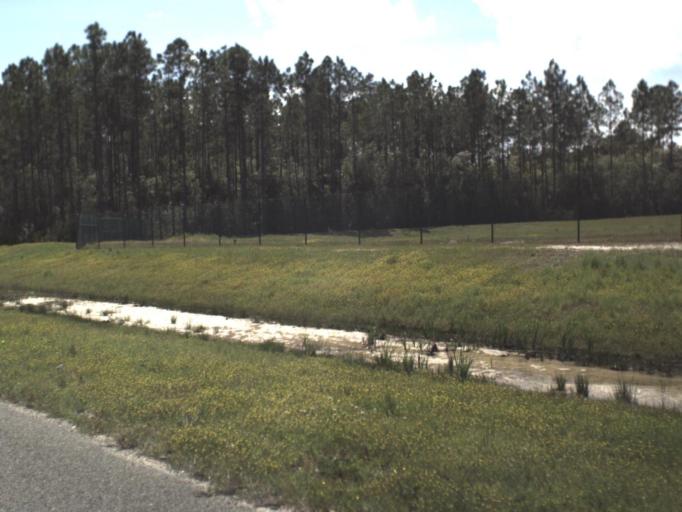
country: US
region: Florida
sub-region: Bay County
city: Laguna Beach
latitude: 30.3658
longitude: -85.8596
